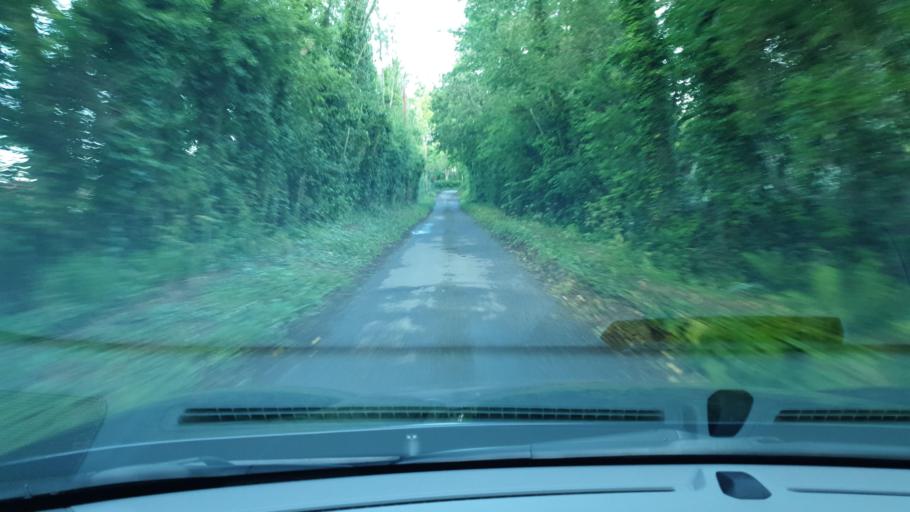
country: IE
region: Leinster
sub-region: An Mhi
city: Ashbourne
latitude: 53.4761
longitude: -6.3391
